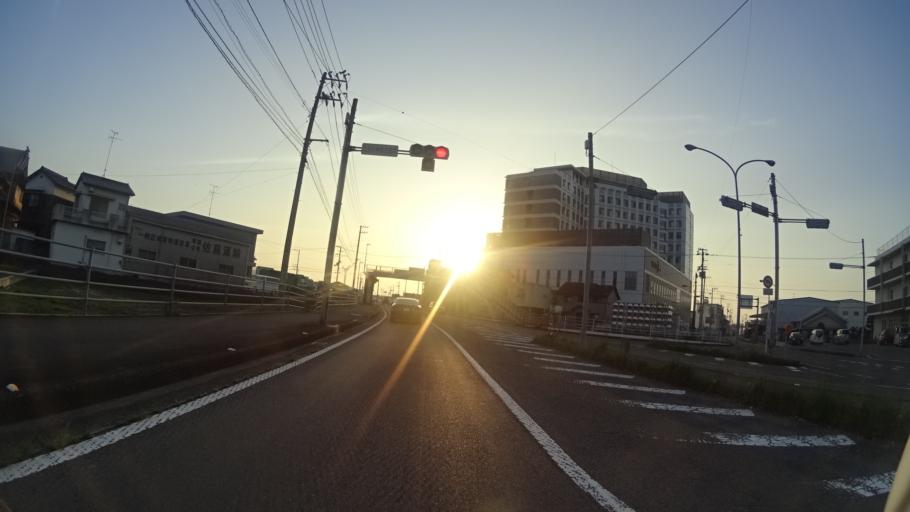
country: JP
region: Ehime
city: Kawanoecho
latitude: 33.9907
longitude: 133.5886
